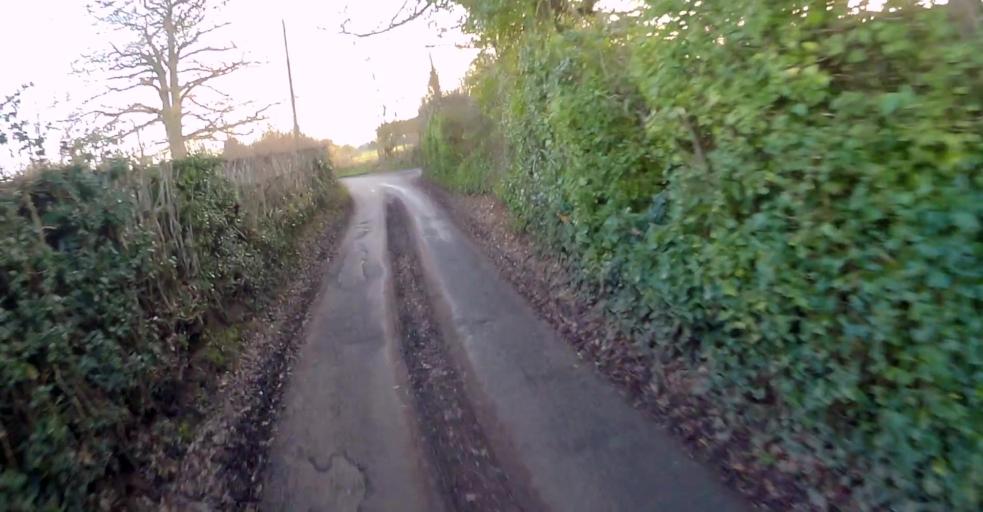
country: GB
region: England
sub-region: Hampshire
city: Hook
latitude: 51.3253
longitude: -0.9904
